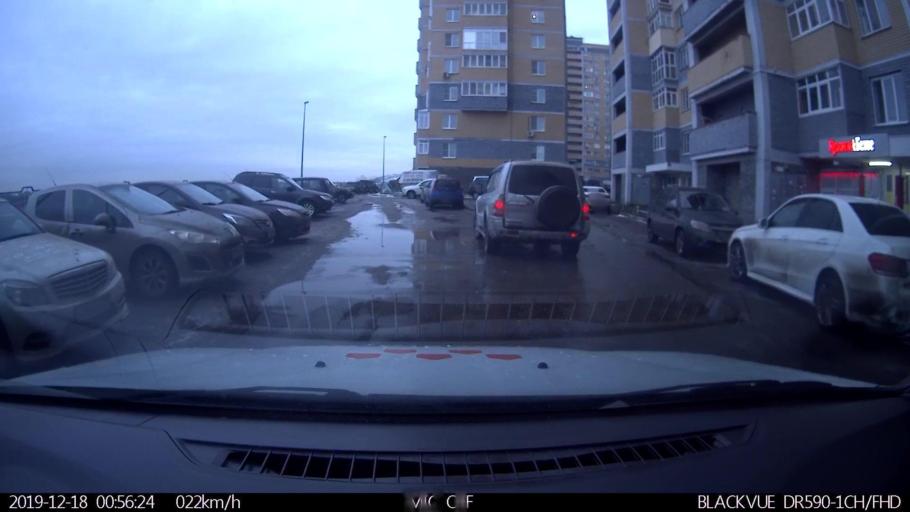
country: RU
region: Nizjnij Novgorod
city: Nizhniy Novgorod
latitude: 56.3492
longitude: 43.9311
